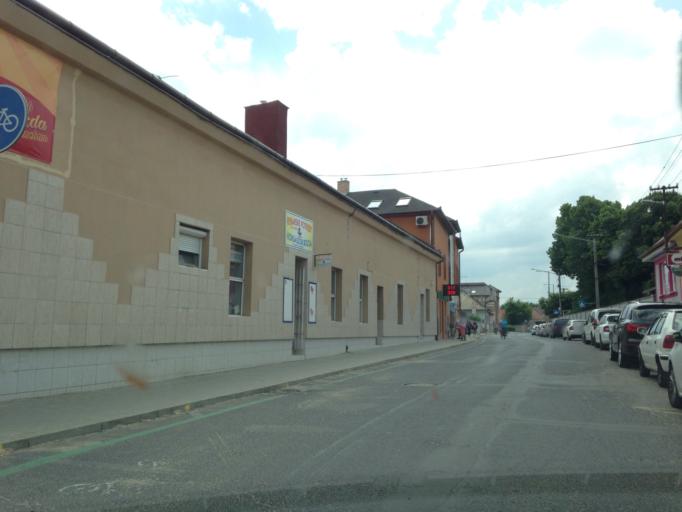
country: SK
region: Nitriansky
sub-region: Okres Nove Zamky
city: Sturovo
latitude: 47.7989
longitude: 18.7211
